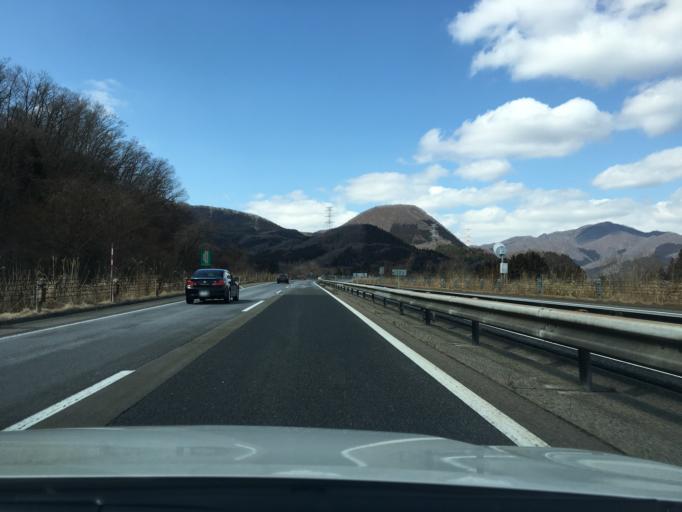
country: JP
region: Miyagi
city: Shiroishi
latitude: 38.1831
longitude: 140.6040
